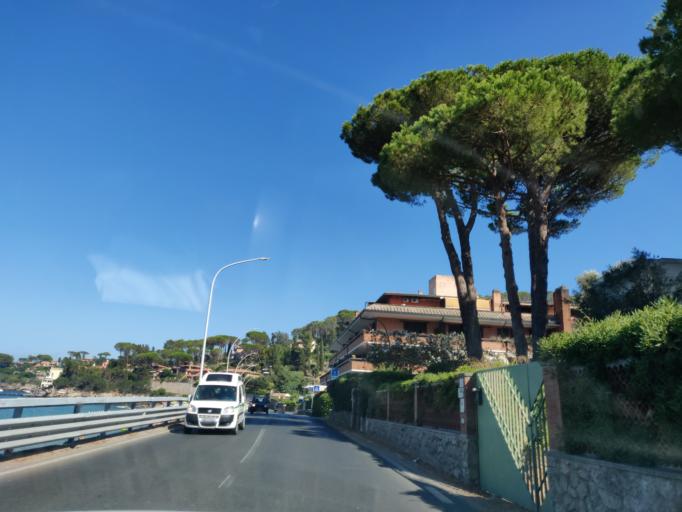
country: IT
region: Tuscany
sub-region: Provincia di Grosseto
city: Monte Argentario
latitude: 42.4339
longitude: 11.1397
